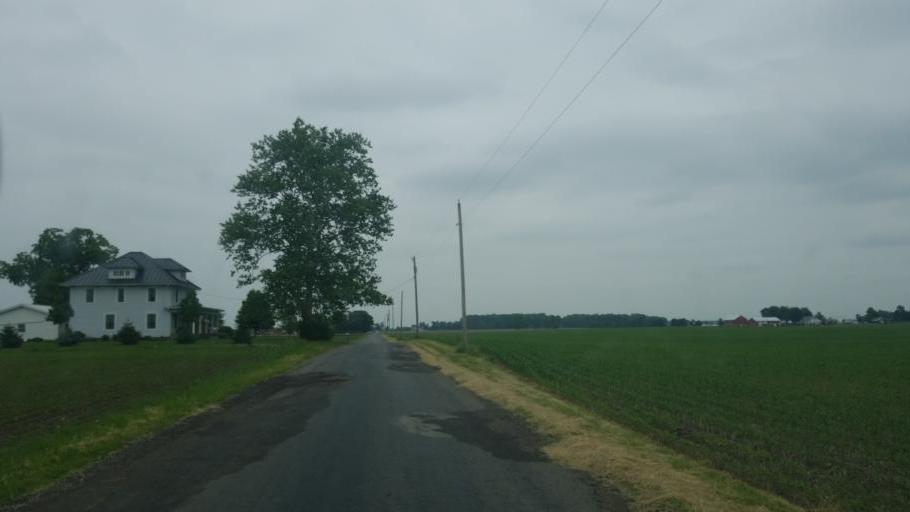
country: US
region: Indiana
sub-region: Elkhart County
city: Wakarusa
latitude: 41.4935
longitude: -86.0682
